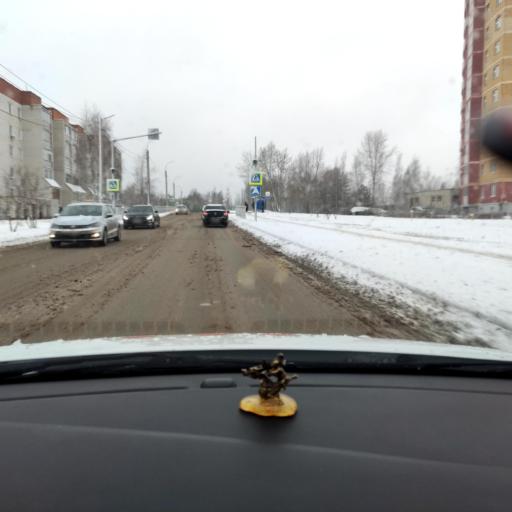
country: RU
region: Tatarstan
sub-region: Zelenodol'skiy Rayon
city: Zelenodolsk
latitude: 55.8599
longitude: 48.5556
